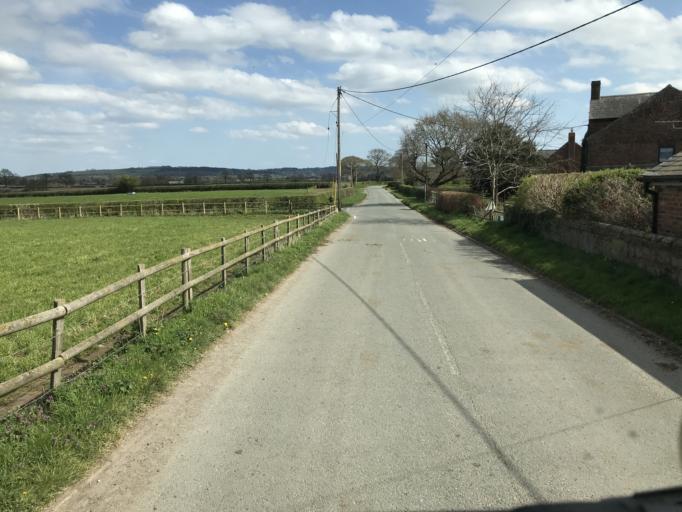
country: GB
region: England
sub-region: Cheshire West and Chester
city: Tarvin
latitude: 53.2117
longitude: -2.7744
